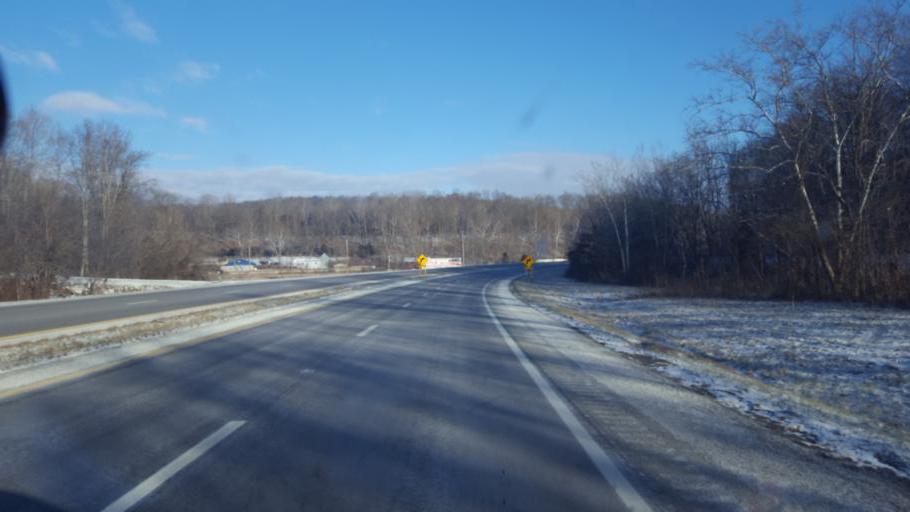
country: US
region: Ohio
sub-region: Ross County
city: Chillicothe
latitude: 39.2442
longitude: -82.9839
